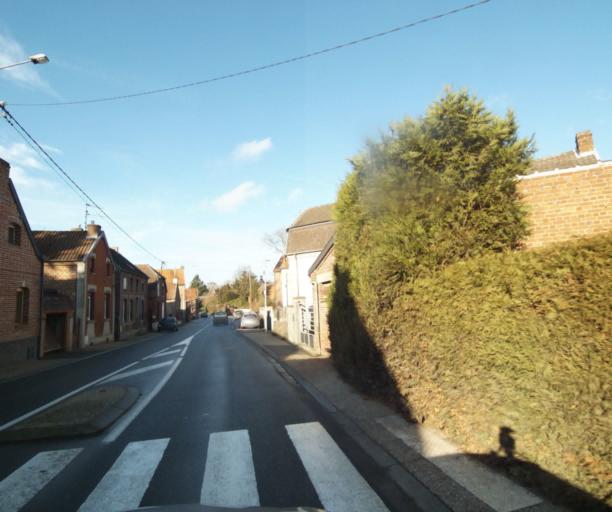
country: FR
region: Nord-Pas-de-Calais
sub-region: Departement du Nord
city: Preseau
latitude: 50.3101
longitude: 3.5791
